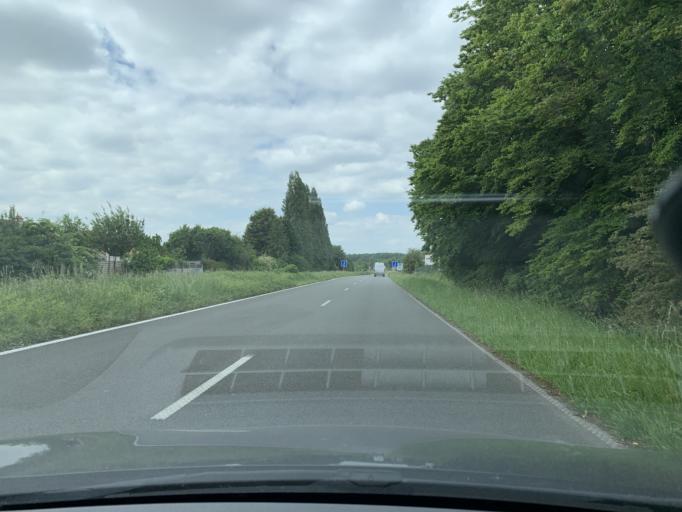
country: FR
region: Nord-Pas-de-Calais
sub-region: Departement du Nord
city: Cuincy
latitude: 50.3799
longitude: 3.0579
